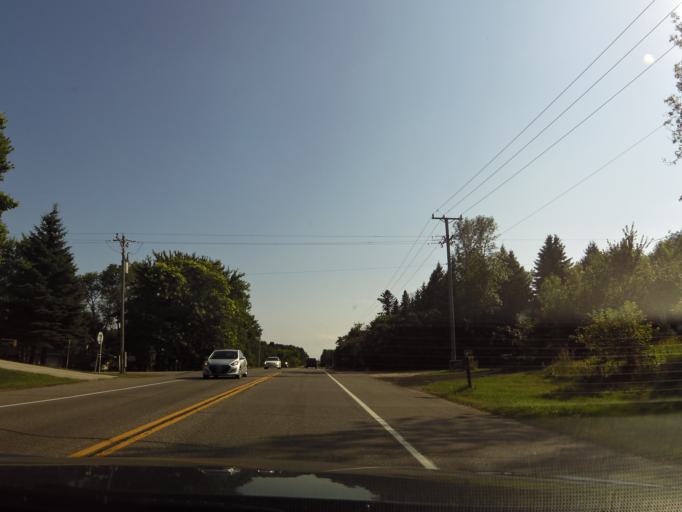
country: US
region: Minnesota
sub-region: Washington County
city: Lake Elmo
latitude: 44.9281
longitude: -92.8626
